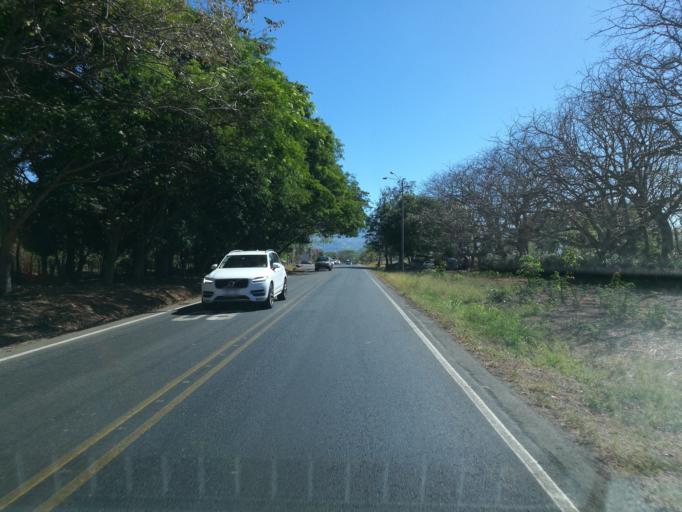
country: CR
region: Puntarenas
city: Miramar
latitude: 10.0934
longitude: -84.8222
